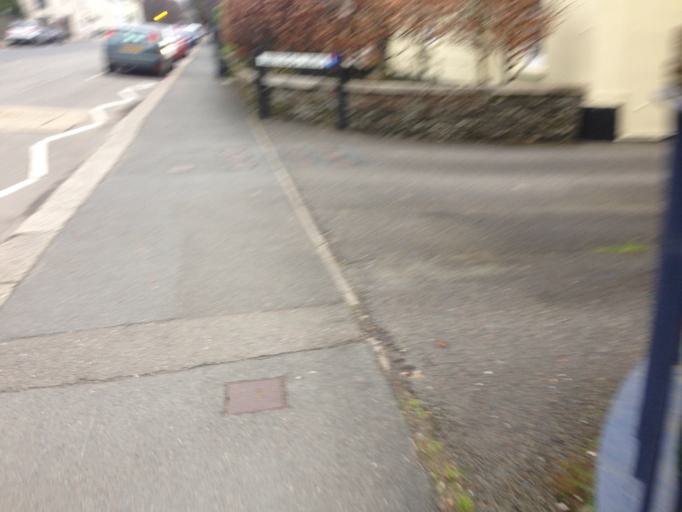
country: GB
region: England
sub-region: Devon
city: Tavistock
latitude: 50.5481
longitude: -4.1472
